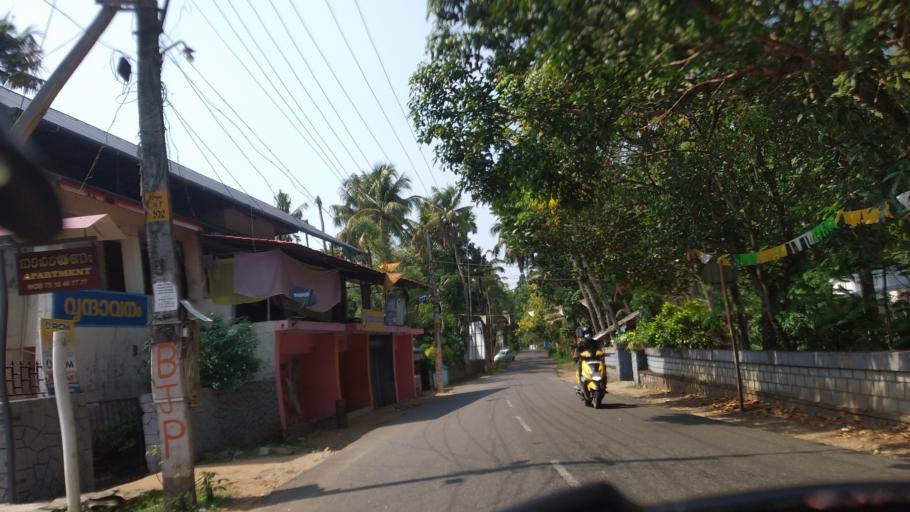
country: IN
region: Kerala
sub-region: Thrissur District
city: Irinjalakuda
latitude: 10.3176
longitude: 76.1254
